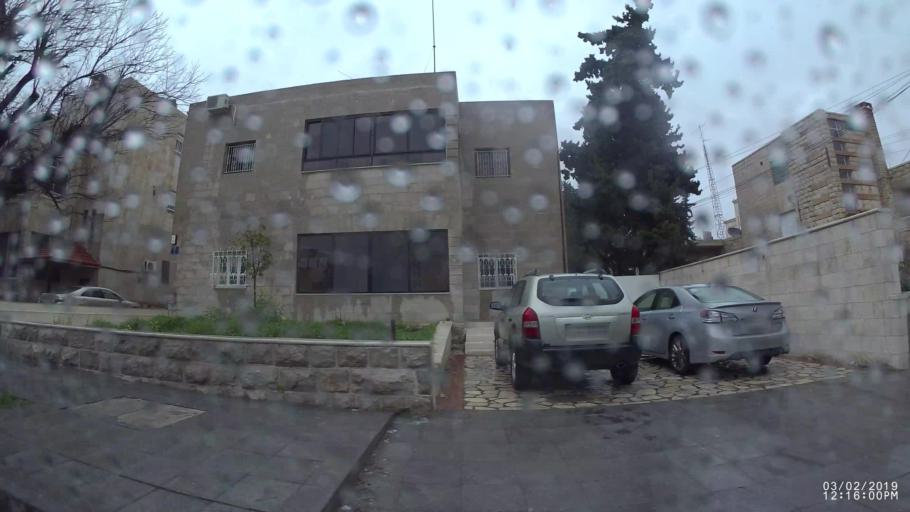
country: JO
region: Amman
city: Amman
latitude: 31.9567
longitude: 35.9162
